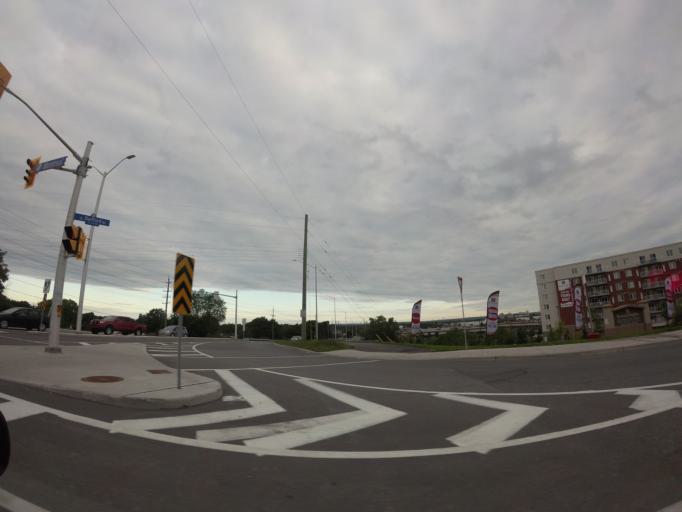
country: CA
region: Ontario
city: Ottawa
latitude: 45.4501
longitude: -75.5880
